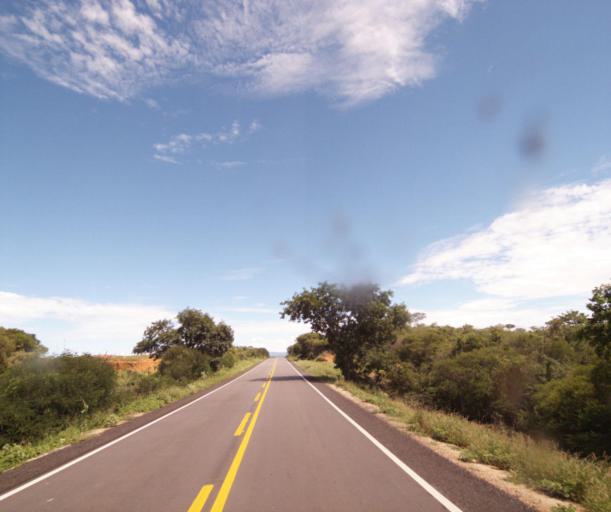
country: BR
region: Bahia
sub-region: Guanambi
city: Guanambi
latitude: -14.3897
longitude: -42.7602
